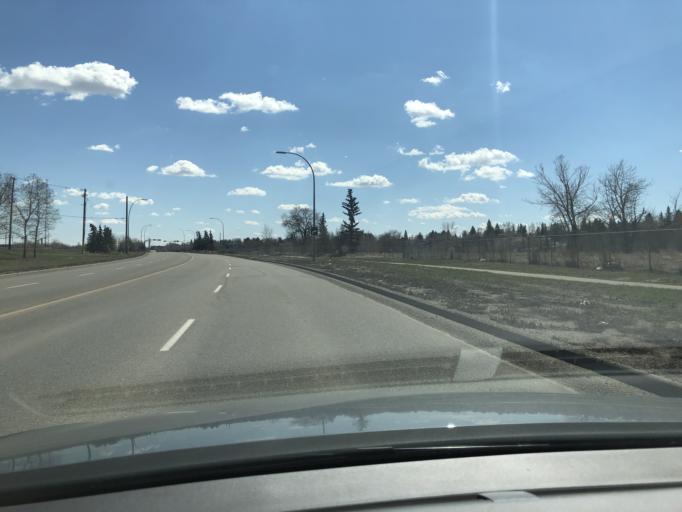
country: CA
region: Alberta
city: Calgary
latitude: 51.0021
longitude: -114.0120
